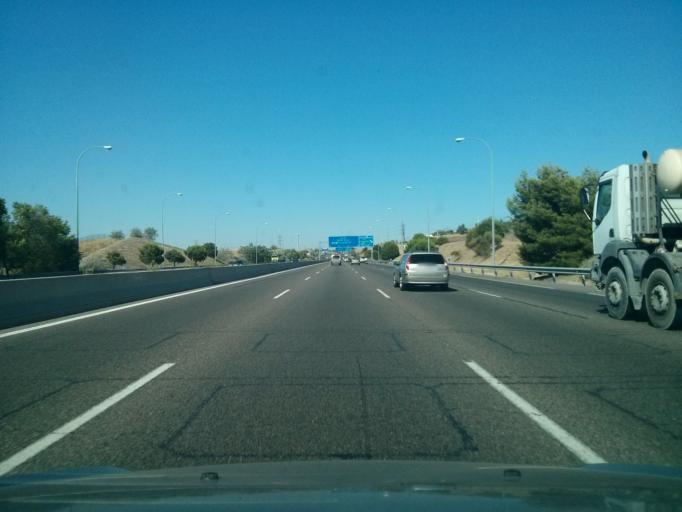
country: ES
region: Madrid
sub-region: Provincia de Madrid
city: Fuencarral-El Pardo
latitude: 40.5081
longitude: -3.7086
